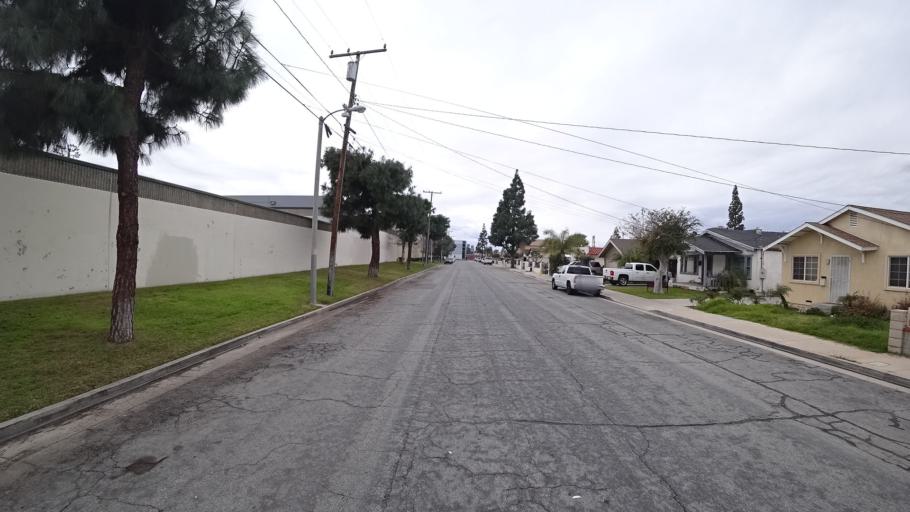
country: US
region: California
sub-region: Orange County
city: Yorba Linda
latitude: 33.8649
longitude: -117.8292
